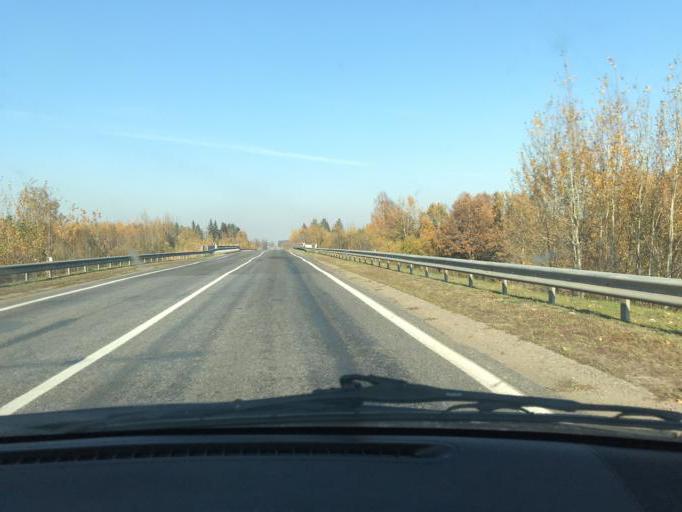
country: BY
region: Vitebsk
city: Orsha
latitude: 54.4323
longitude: 30.4807
